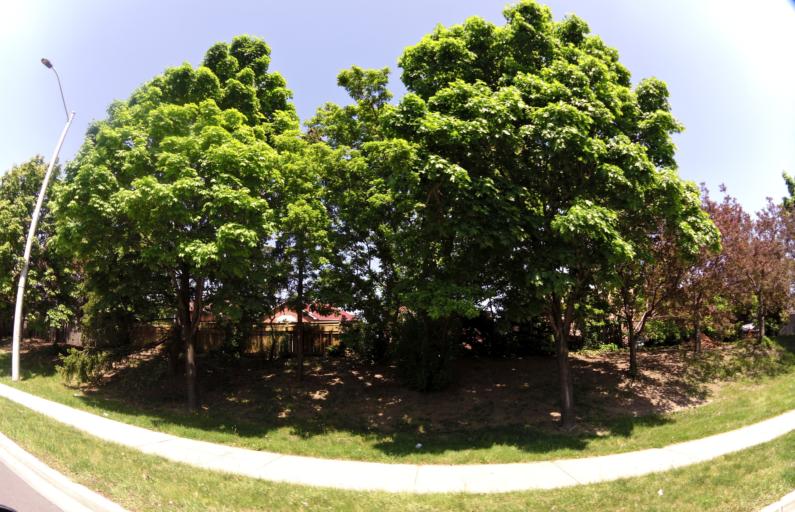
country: CA
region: Ontario
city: Mississauga
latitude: 43.6149
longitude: -79.6402
